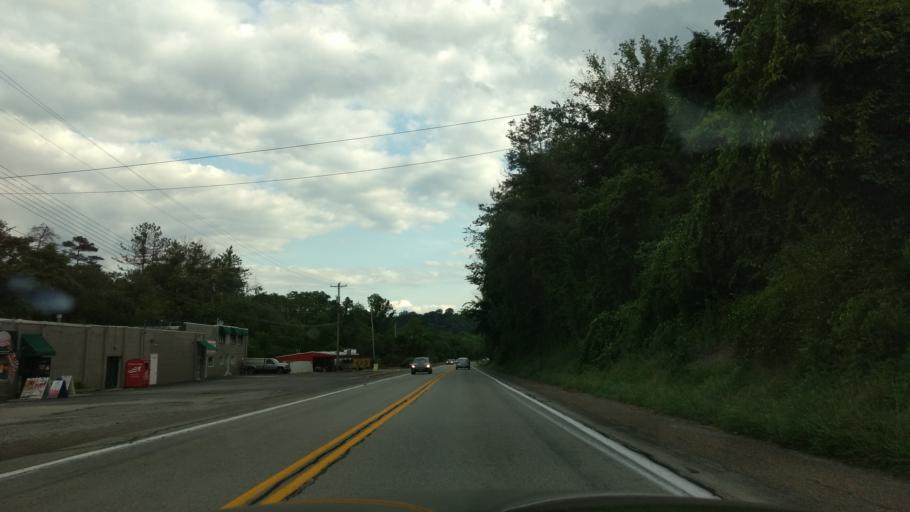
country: US
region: Pennsylvania
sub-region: Westmoreland County
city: Murrysville
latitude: 40.4702
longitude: -79.7064
